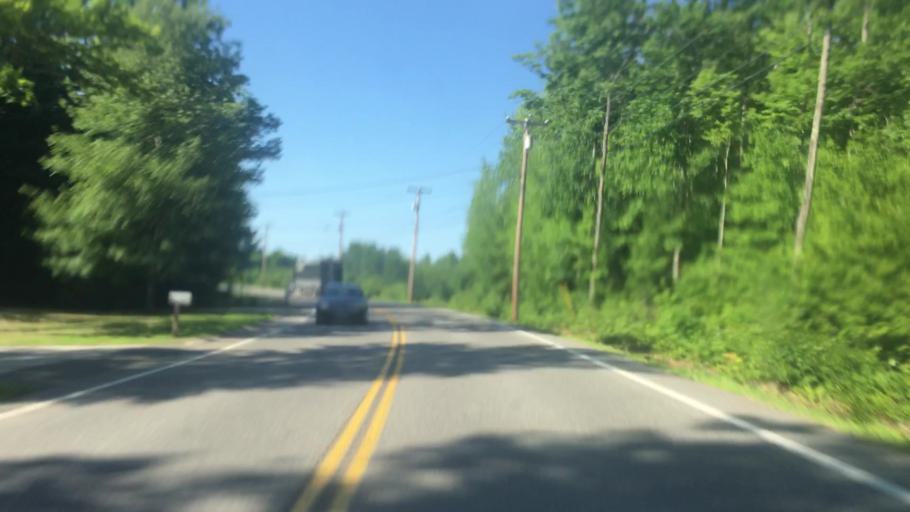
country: US
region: Maine
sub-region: York County
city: Dayton
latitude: 43.5611
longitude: -70.4982
